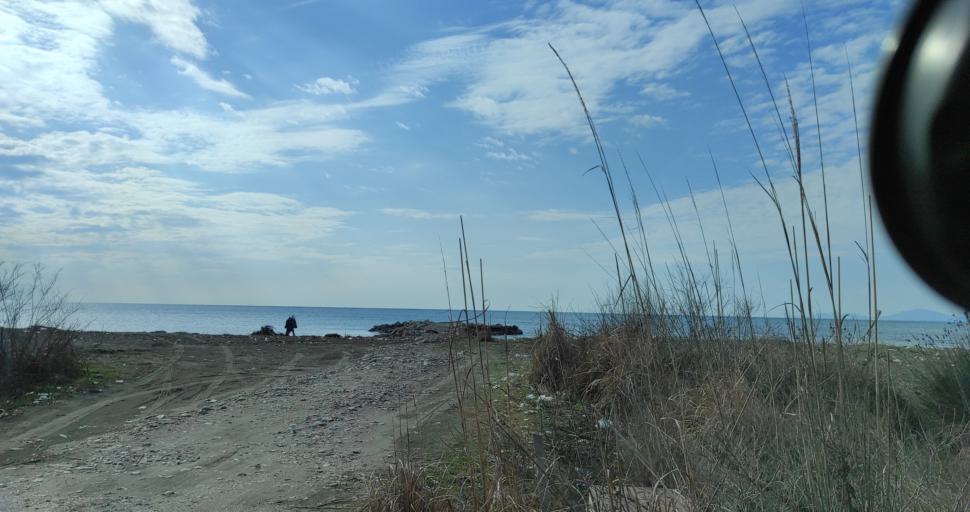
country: AL
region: Lezhe
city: Shengjin
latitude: 41.7847
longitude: 19.6032
